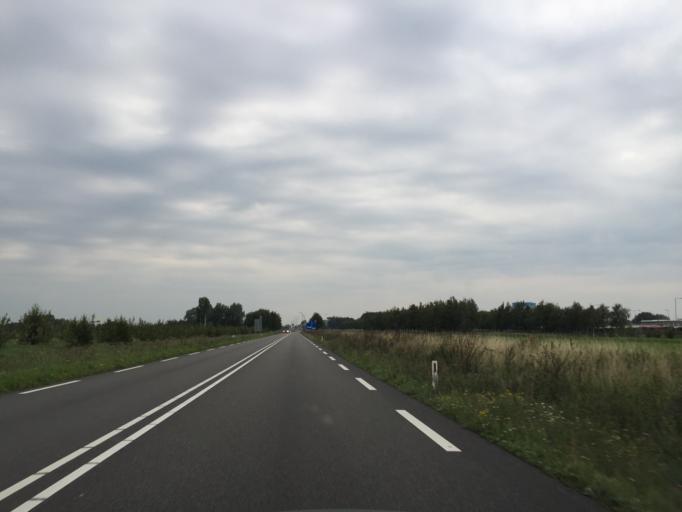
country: NL
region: North Holland
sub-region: Gemeente Amstelveen
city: Amstelveen
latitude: 52.3190
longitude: 4.8022
